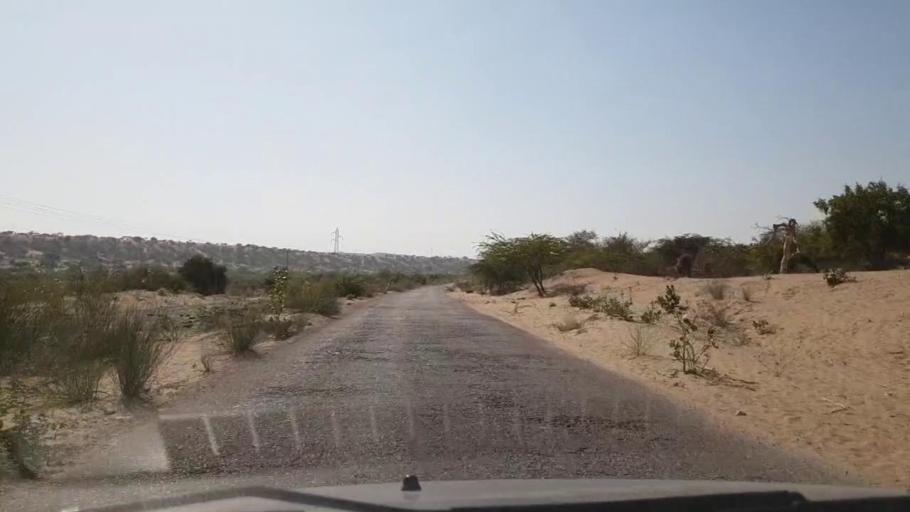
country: PK
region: Sindh
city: Diplo
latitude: 24.5392
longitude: 69.6436
